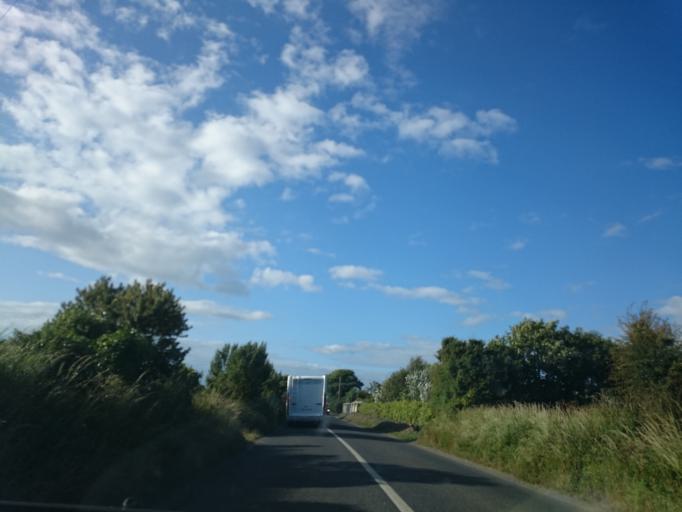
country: IE
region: Leinster
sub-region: Loch Garman
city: Loch Garman
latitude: 52.1924
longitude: -6.5596
